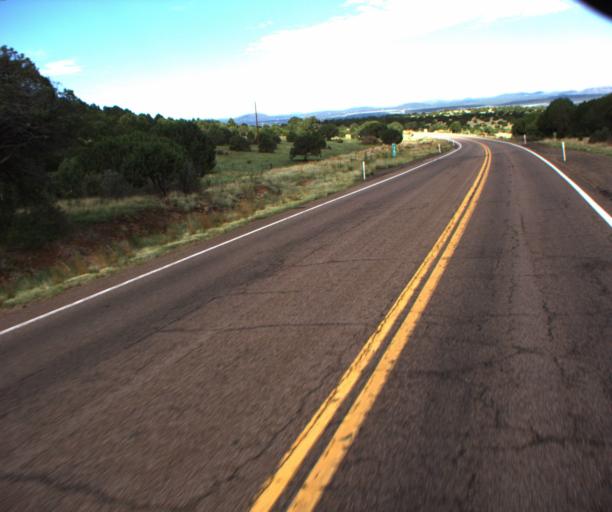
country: US
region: Arizona
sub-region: Apache County
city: Saint Johns
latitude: 34.2684
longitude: -109.5930
